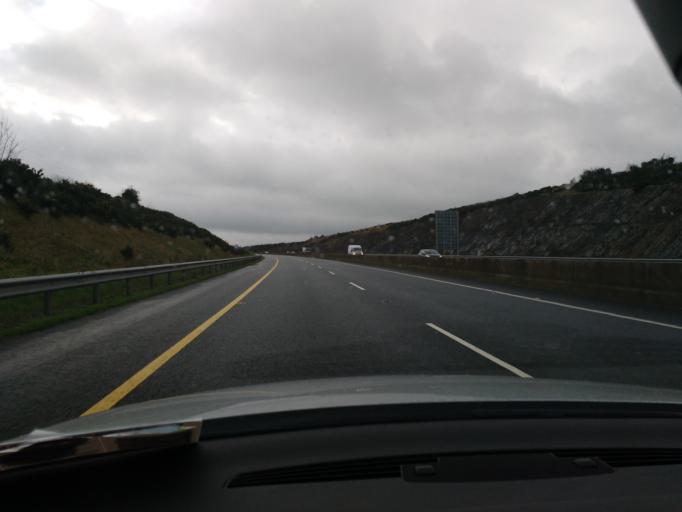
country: IE
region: Munster
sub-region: North Tipperary
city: Nenagh
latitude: 52.8420
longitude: -8.2741
